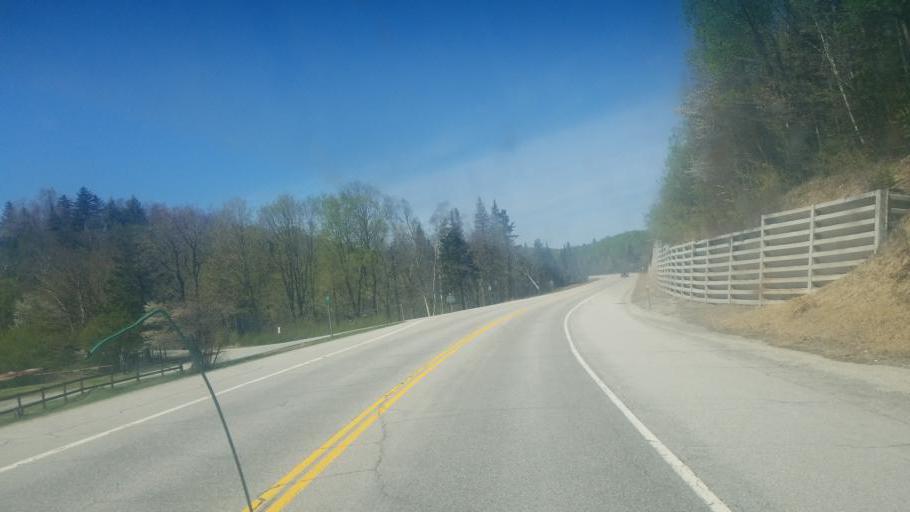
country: US
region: New Hampshire
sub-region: Grafton County
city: Deerfield
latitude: 44.2652
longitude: -71.4984
